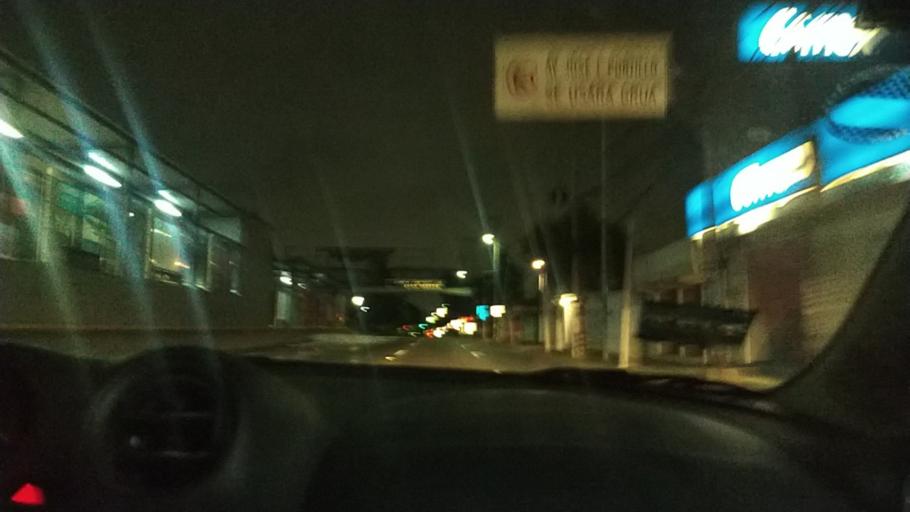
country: MX
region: Mexico
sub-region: Tultitlan
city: Fuentes del Valle
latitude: 19.6290
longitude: -99.1357
